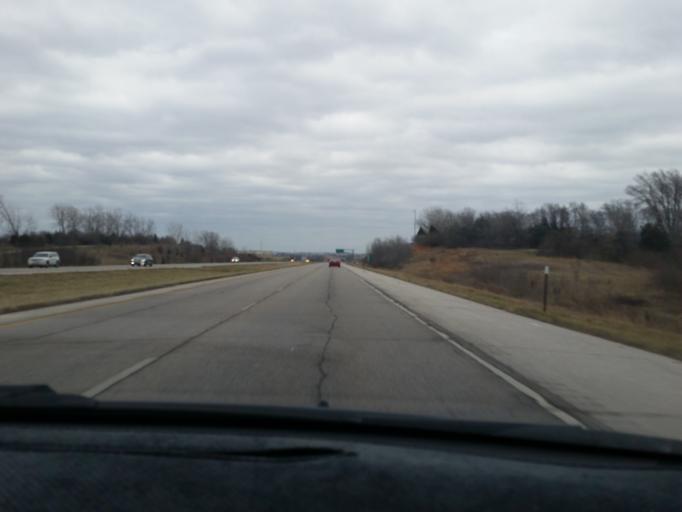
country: US
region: Kansas
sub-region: Johnson County
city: Olathe
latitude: 38.9415
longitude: -94.8244
